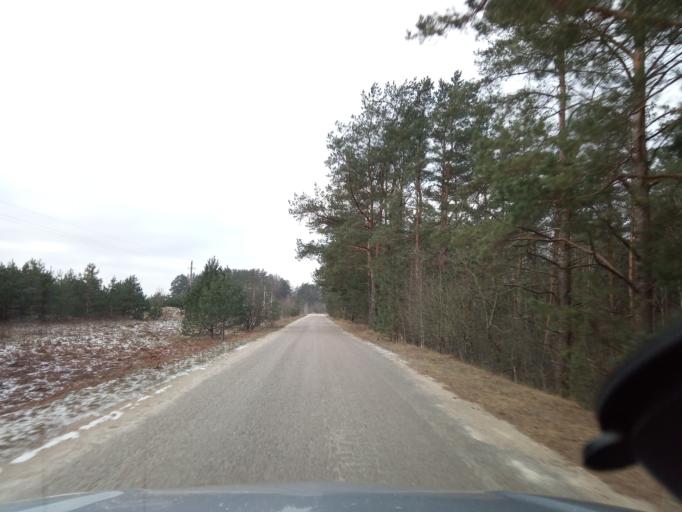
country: LT
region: Alytaus apskritis
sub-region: Alytaus rajonas
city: Daugai
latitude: 54.3270
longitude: 24.3048
